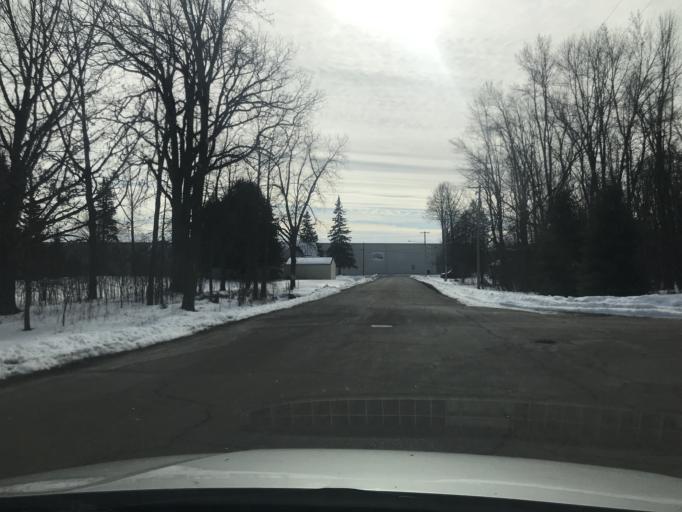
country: US
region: Wisconsin
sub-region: Oconto County
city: Gillett
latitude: 44.8963
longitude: -88.2972
